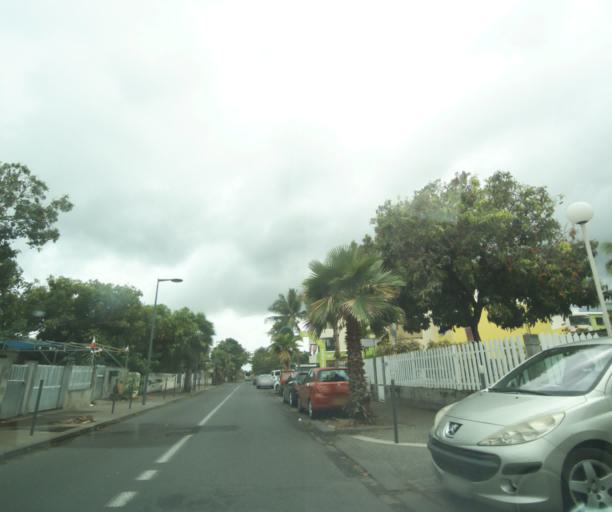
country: RE
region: Reunion
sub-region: Reunion
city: Saint-Paul
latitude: -20.9950
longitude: 55.2844
